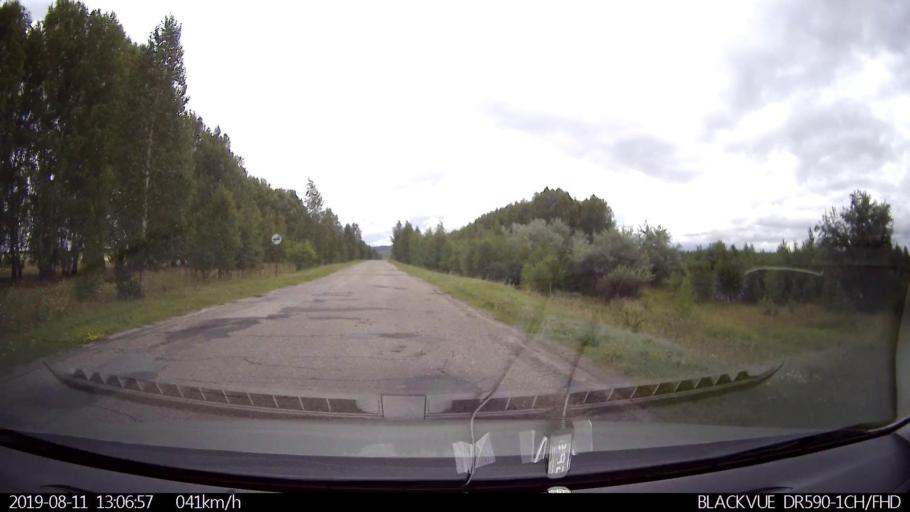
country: RU
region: Ulyanovsk
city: Ignatovka
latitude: 53.8662
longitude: 47.6394
